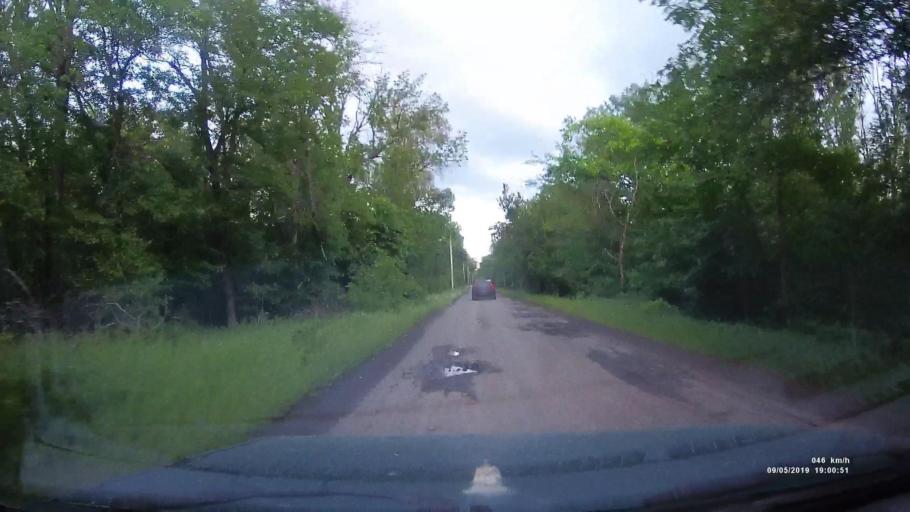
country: RU
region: Krasnodarskiy
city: Kanelovskaya
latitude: 46.7502
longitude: 39.1396
